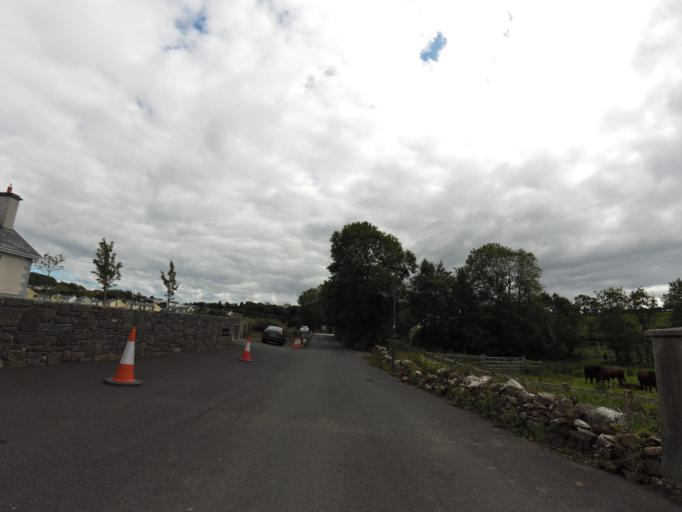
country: IE
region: Connaught
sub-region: Maigh Eo
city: Westport
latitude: 53.8102
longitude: -9.5270
